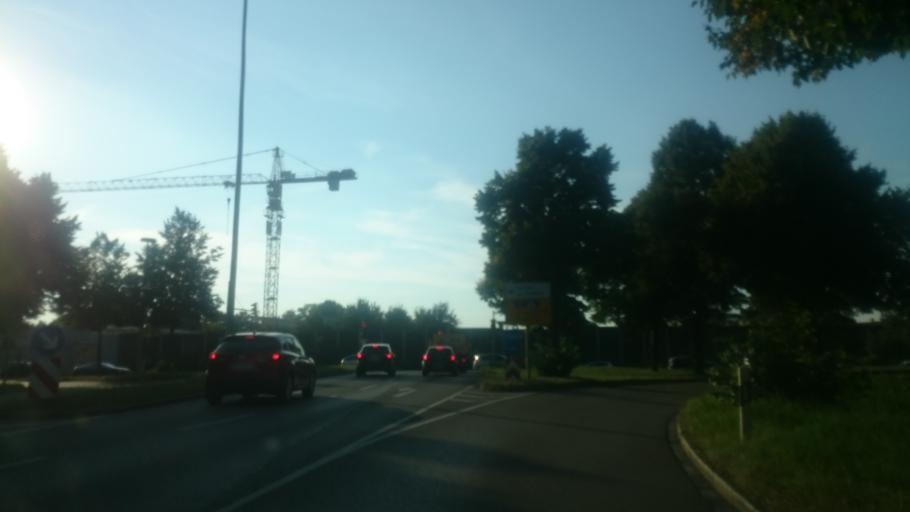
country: DE
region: Bavaria
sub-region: Swabia
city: Augsburg
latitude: 48.3968
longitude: 10.9211
